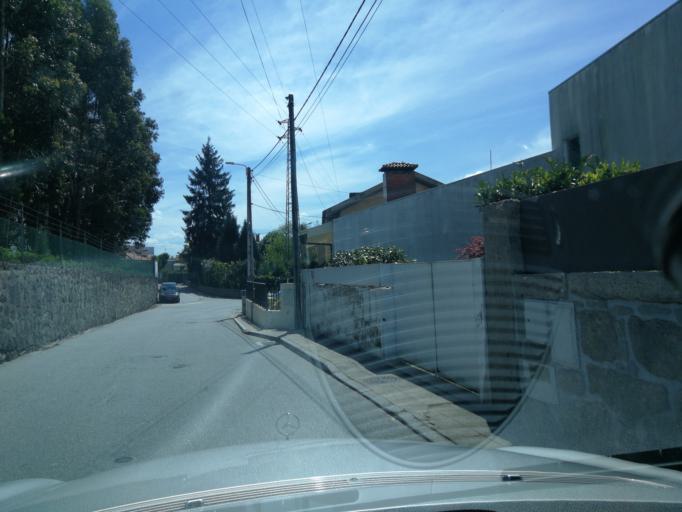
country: PT
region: Braga
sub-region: Vila Nova de Famalicao
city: Vila Nova de Famalicao
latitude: 41.4204
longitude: -8.5134
